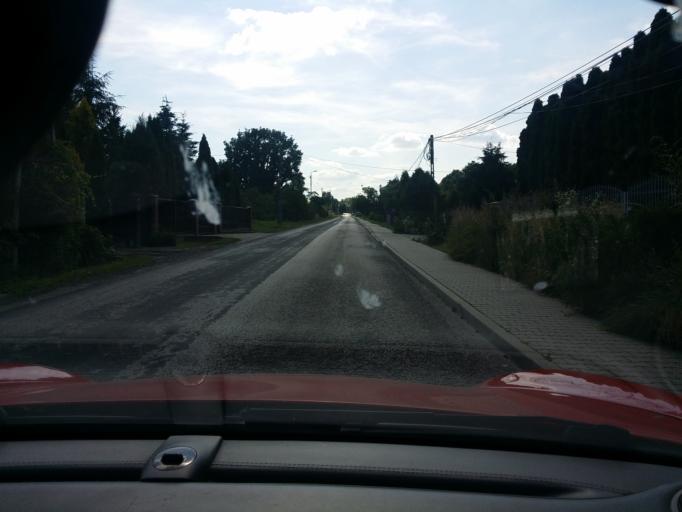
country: PL
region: Masovian Voivodeship
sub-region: Powiat radomski
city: Trablice
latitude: 51.3504
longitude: 21.1187
